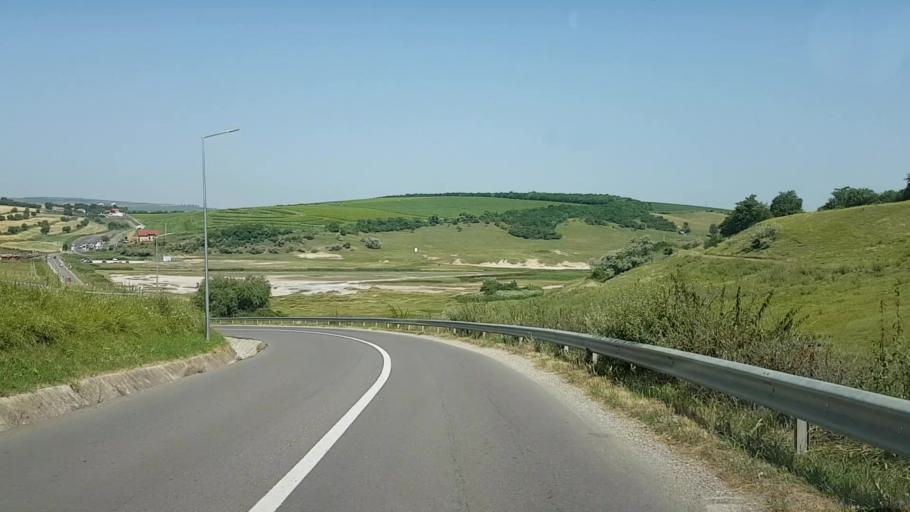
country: RO
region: Cluj
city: Turda
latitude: 46.5867
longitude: 23.7951
